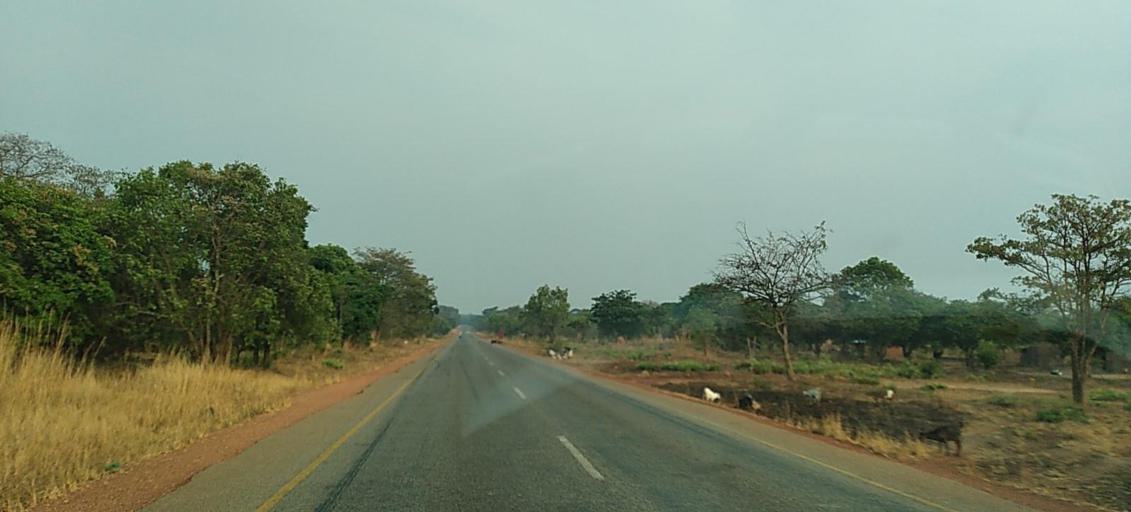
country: ZM
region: North-Western
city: Solwezi
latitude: -12.3871
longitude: 26.0316
